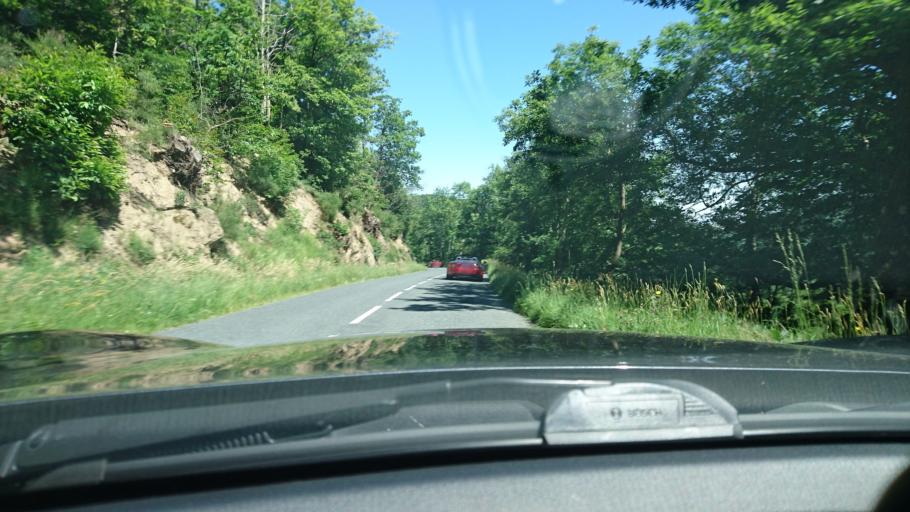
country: FR
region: Rhone-Alpes
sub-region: Departement du Rhone
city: Courzieu
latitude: 45.7174
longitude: 4.6012
